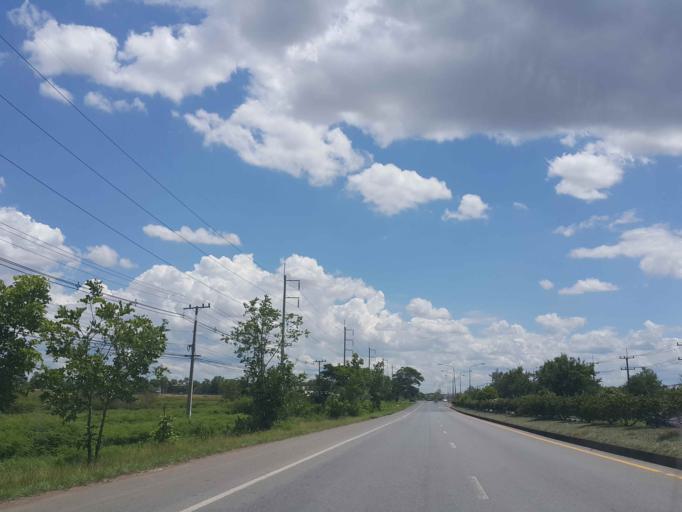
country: TH
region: Phrae
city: Nong Muang Khai
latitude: 18.2396
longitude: 100.2179
